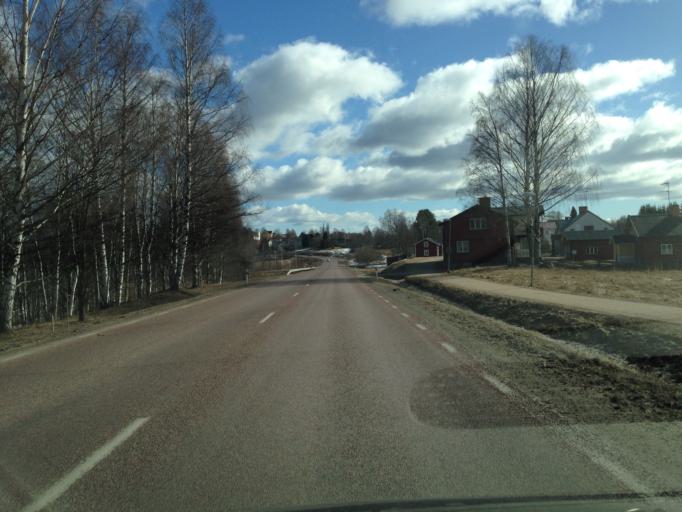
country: SE
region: Gaevleborg
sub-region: Ljusdals Kommun
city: Farila
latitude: 61.7984
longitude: 15.8216
